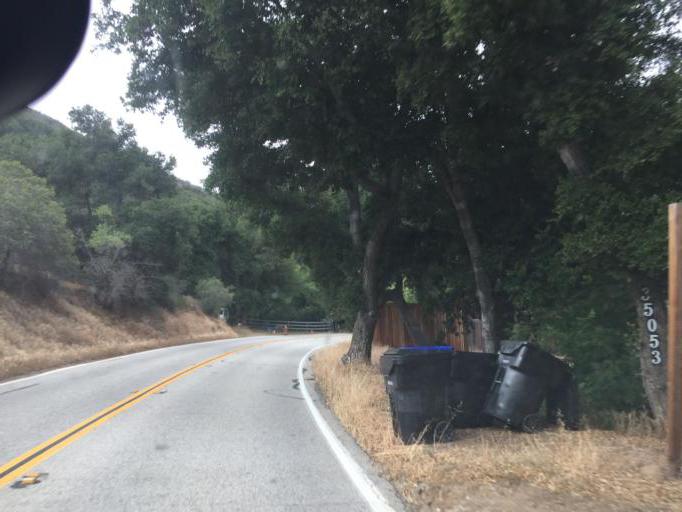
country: US
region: California
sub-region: Los Angeles County
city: Green Valley
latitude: 34.5708
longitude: -118.3901
